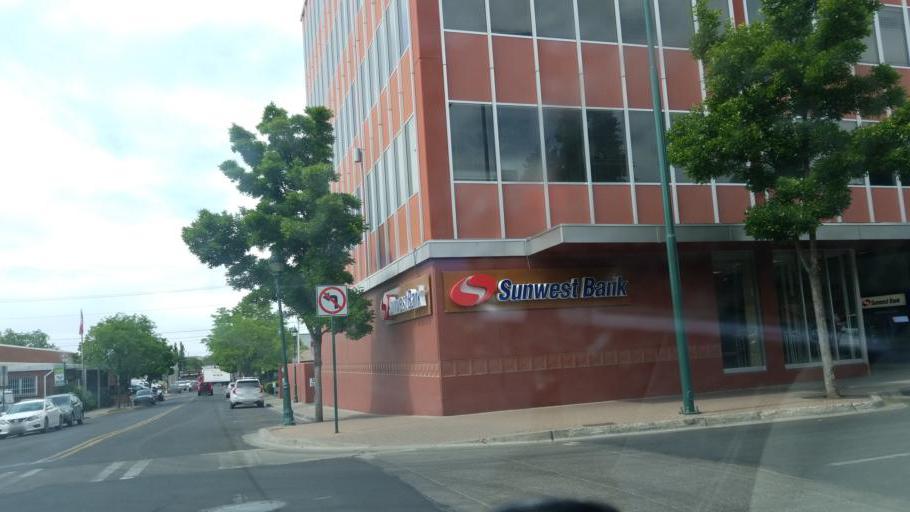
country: US
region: Arizona
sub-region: Coconino County
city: Flagstaff
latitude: 35.1988
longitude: -111.6461
